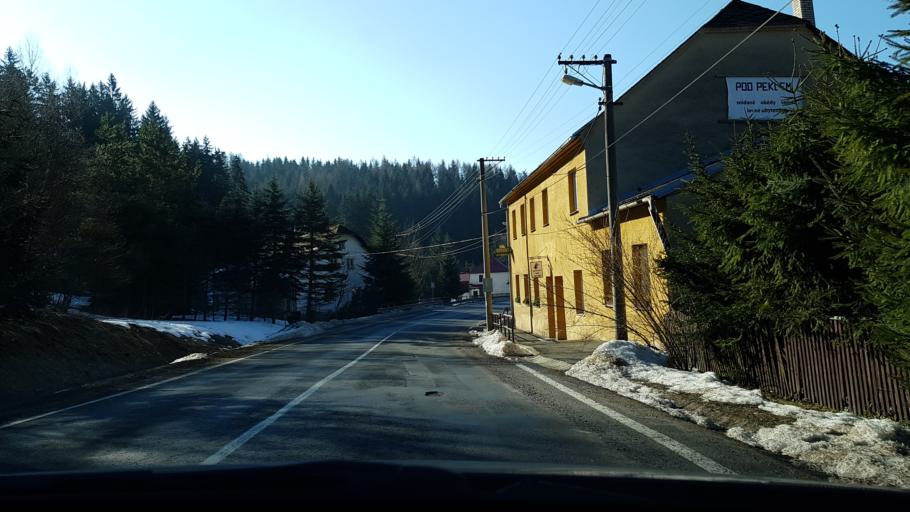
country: CZ
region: Olomoucky
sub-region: Okres Sumperk
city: Stare Mesto
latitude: 50.1136
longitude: 17.0053
